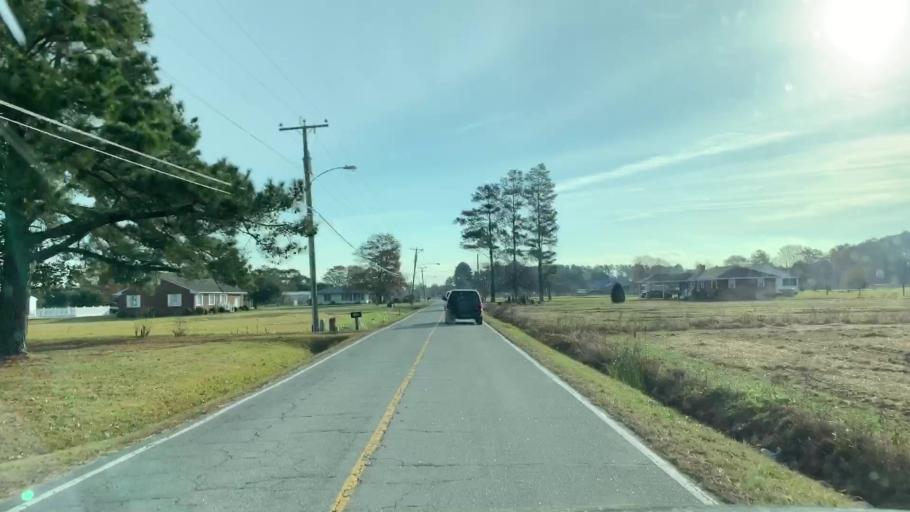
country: US
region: Virginia
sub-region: City of Virginia Beach
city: Virginia Beach
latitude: 36.6910
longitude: -76.0137
